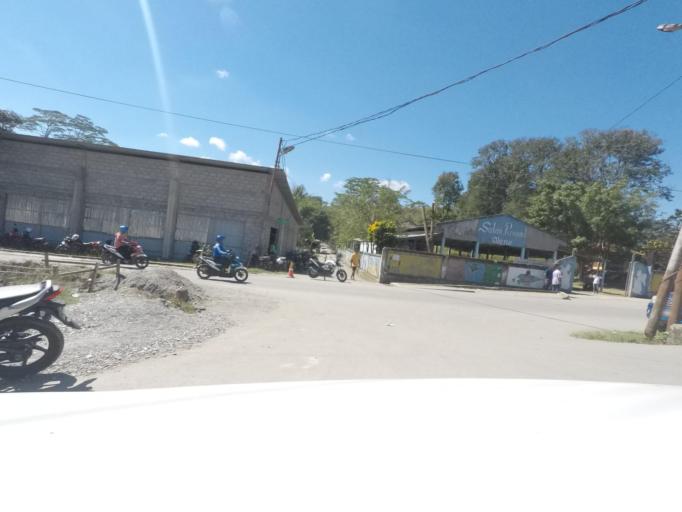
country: TL
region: Ermera
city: Gleno
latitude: -8.7213
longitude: 125.4361
